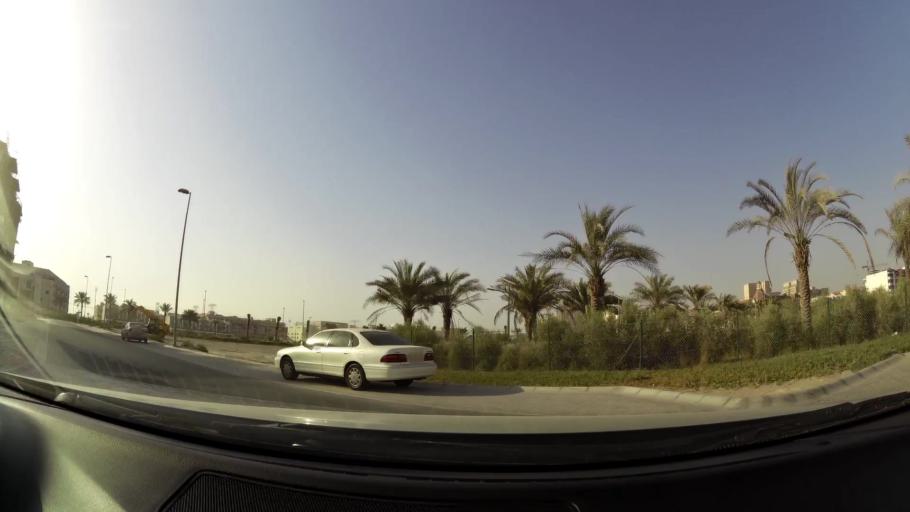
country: AE
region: Dubai
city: Dubai
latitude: 25.0619
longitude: 55.2047
